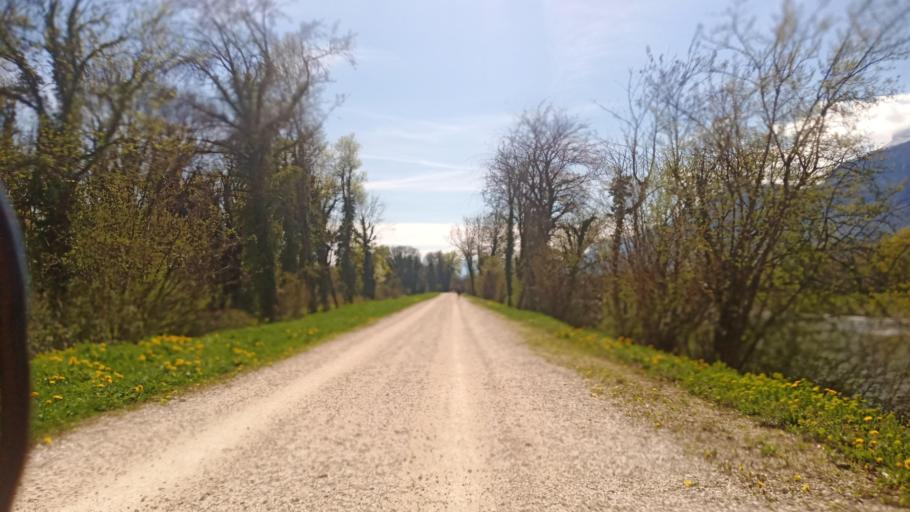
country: FR
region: Rhone-Alpes
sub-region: Departement de l'Isere
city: Tencin
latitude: 45.3205
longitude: 5.9533
